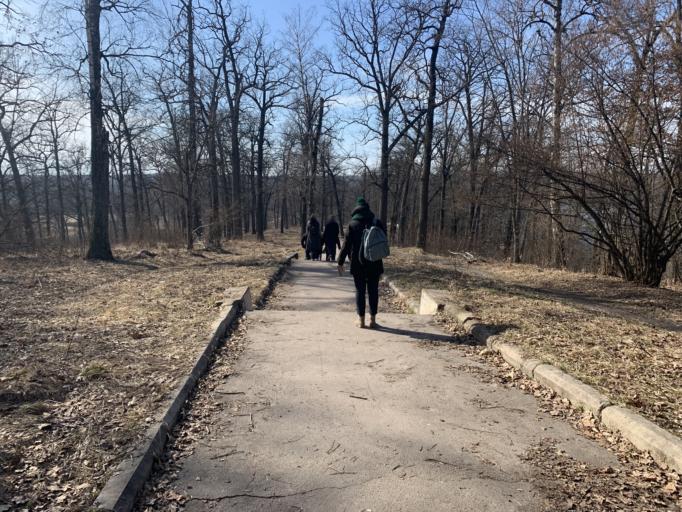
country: RU
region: Kursk
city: Zheleznogorsk
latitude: 52.3201
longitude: 35.3646
